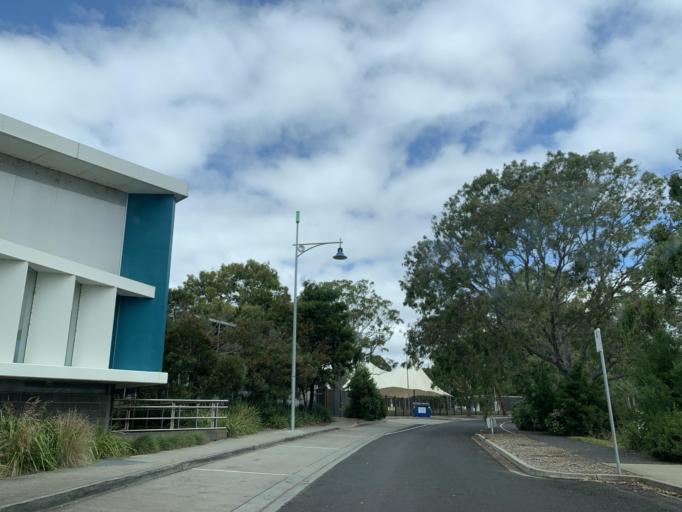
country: AU
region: Victoria
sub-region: Wellington
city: Sale
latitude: -38.1118
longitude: 147.0791
